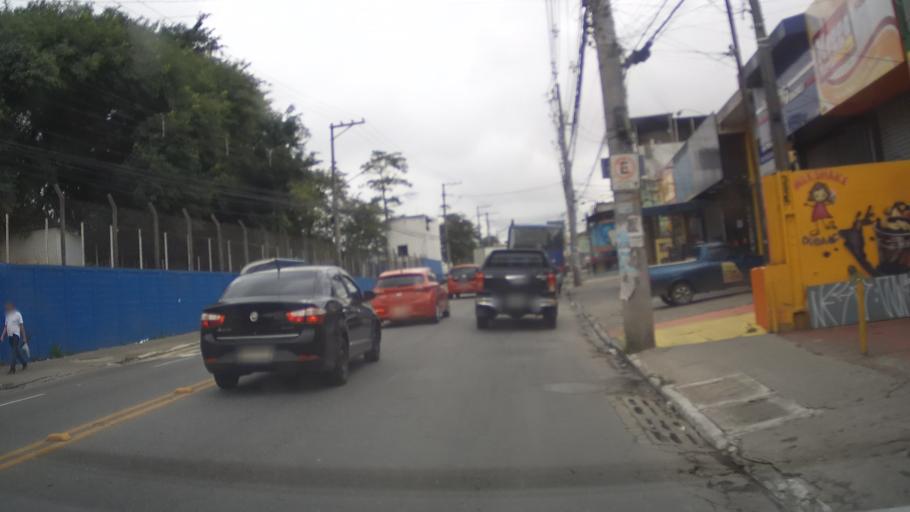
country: BR
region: Sao Paulo
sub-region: Guarulhos
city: Guarulhos
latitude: -23.4322
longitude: -46.5036
